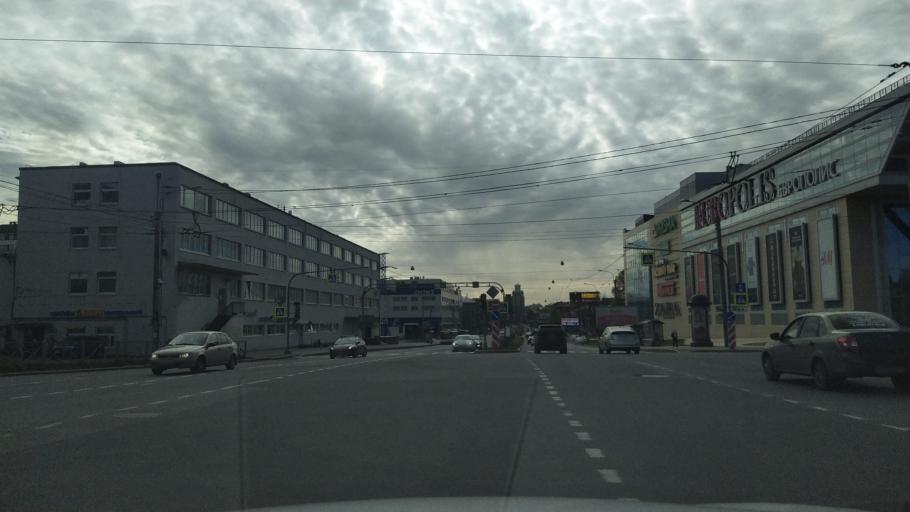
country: RU
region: St.-Petersburg
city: Kushelevka
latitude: 59.9869
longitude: 30.3576
